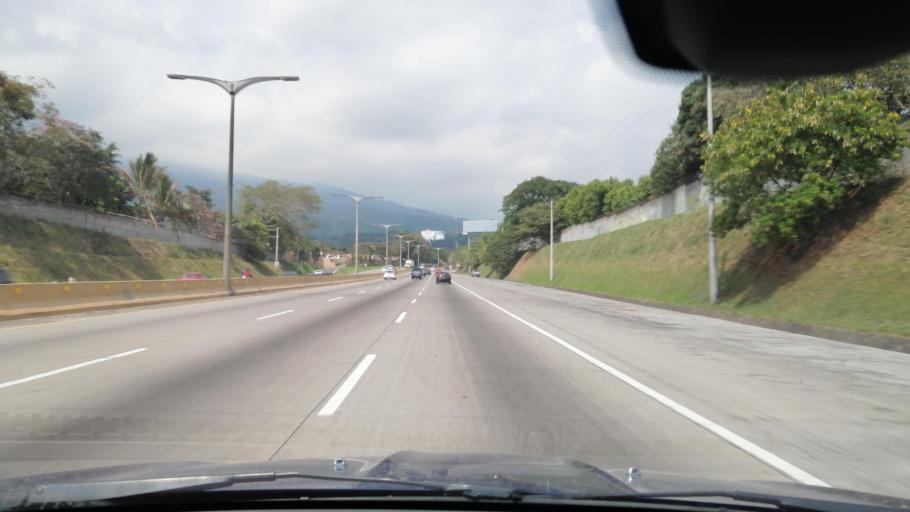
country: SV
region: La Libertad
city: Santa Tecla
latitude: 13.6826
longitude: -89.2983
